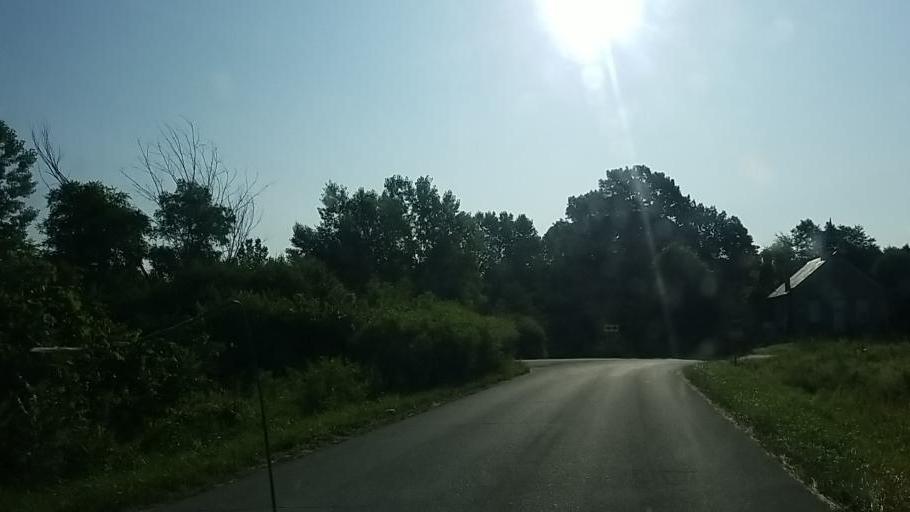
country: US
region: Michigan
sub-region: Newaygo County
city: Newaygo
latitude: 43.3656
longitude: -85.8215
